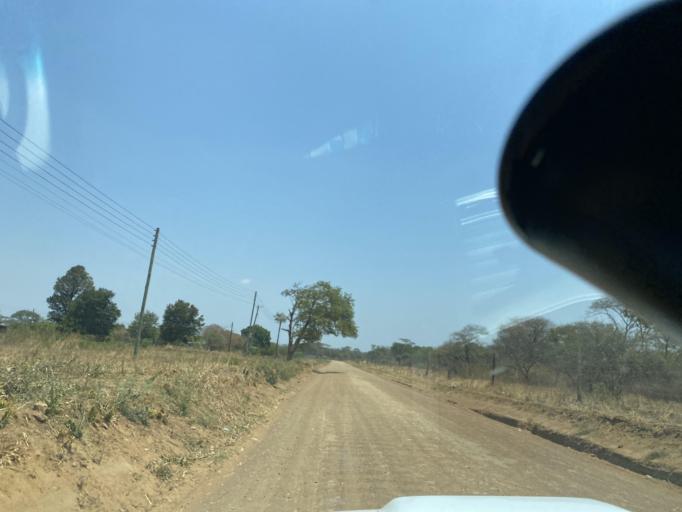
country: ZM
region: Lusaka
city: Lusaka
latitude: -15.4319
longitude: 28.0831
